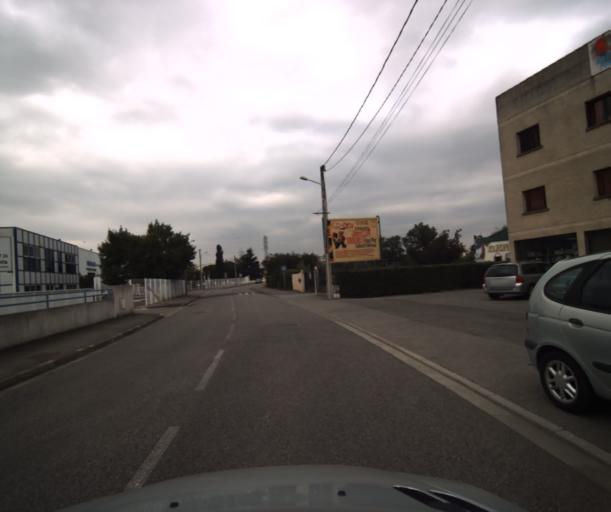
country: FR
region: Midi-Pyrenees
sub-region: Departement de la Haute-Garonne
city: Portet-sur-Garonne
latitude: 43.5392
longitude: 1.4023
